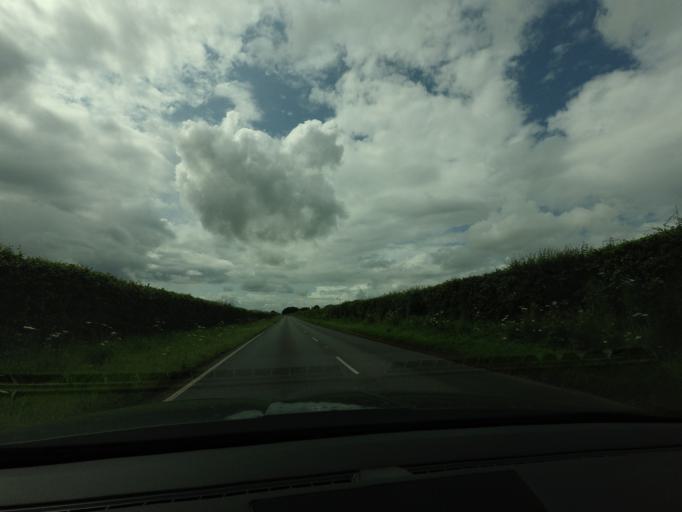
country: GB
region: Scotland
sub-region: Aberdeenshire
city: Whitehills
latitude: 57.6568
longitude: -2.6053
